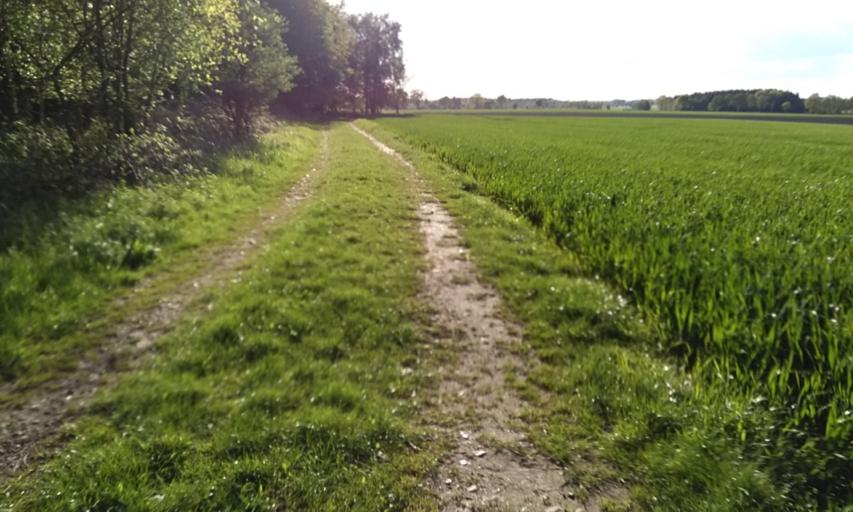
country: DE
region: Lower Saxony
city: Sauensiek
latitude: 53.4046
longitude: 9.5880
